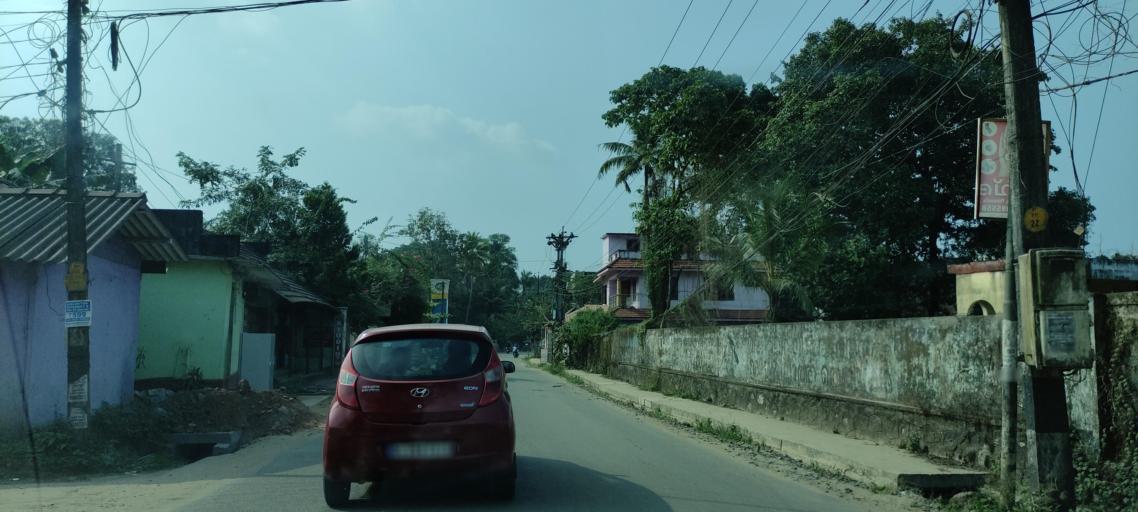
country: IN
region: Kerala
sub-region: Pattanamtitta
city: Tiruvalla
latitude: 9.3787
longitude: 76.5639
